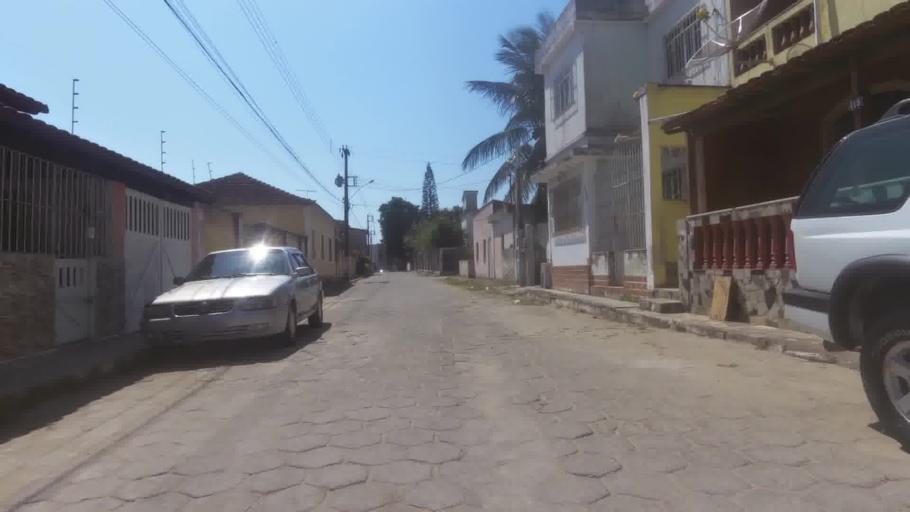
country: BR
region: Espirito Santo
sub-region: Itapemirim
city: Itapemirim
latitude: -21.0087
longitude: -40.8131
